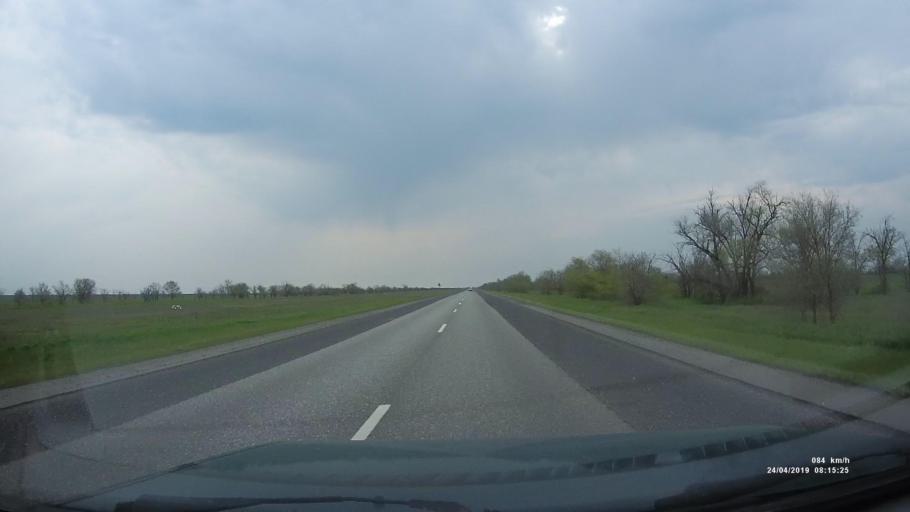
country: RU
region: Kalmykiya
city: Priyutnoye
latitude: 46.0999
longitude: 43.5934
